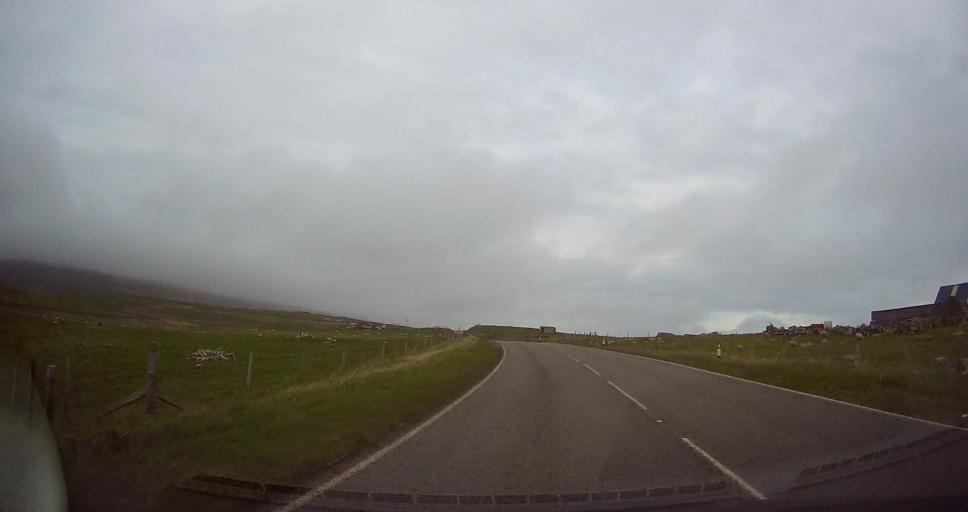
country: GB
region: Scotland
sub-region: Shetland Islands
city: Sandwick
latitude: 59.9305
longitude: -1.2958
